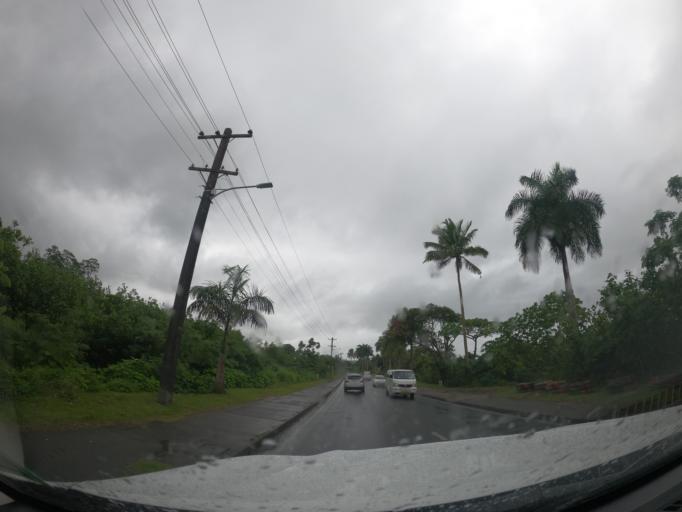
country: FJ
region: Central
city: Suva
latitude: -18.1133
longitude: 178.4189
